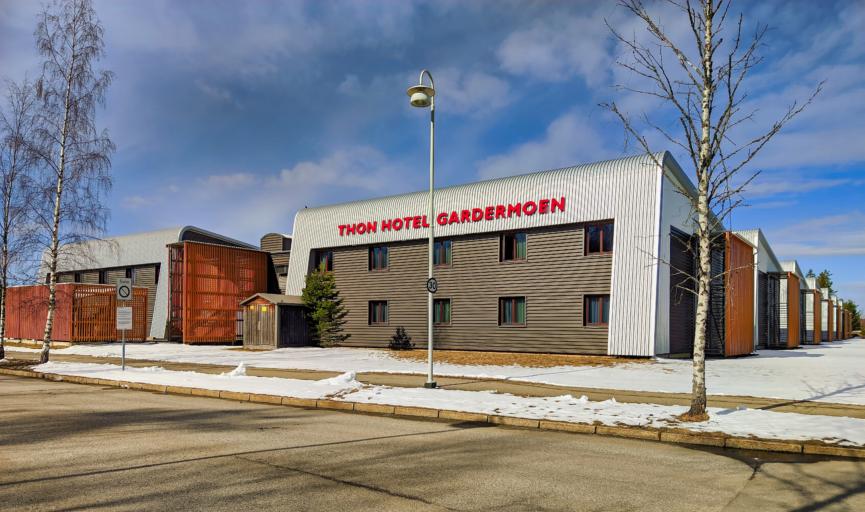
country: NO
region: Akershus
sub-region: Ullensaker
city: Jessheim
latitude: 60.1676
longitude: 11.1482
